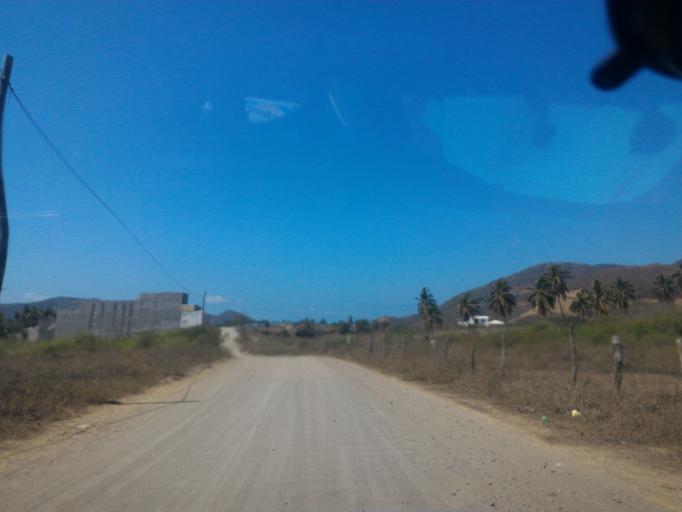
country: MX
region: Michoacan
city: Coahuayana Viejo
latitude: 18.5872
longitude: -103.6803
